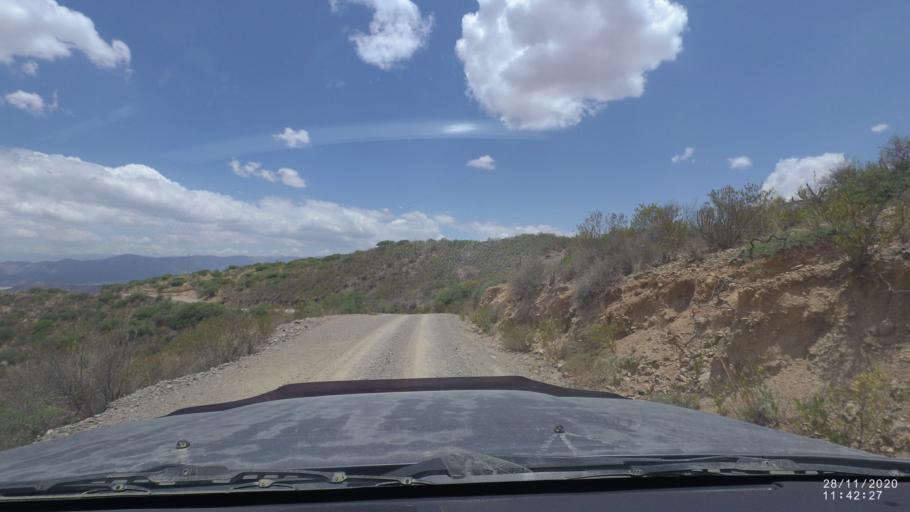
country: BO
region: Cochabamba
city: Tarata
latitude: -17.6647
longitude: -66.0465
